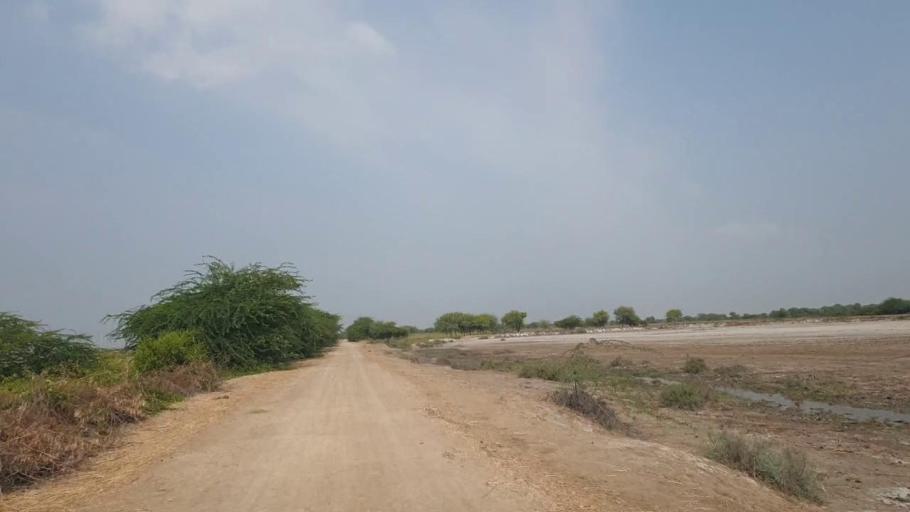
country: PK
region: Sindh
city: Badin
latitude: 24.5551
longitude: 68.7313
